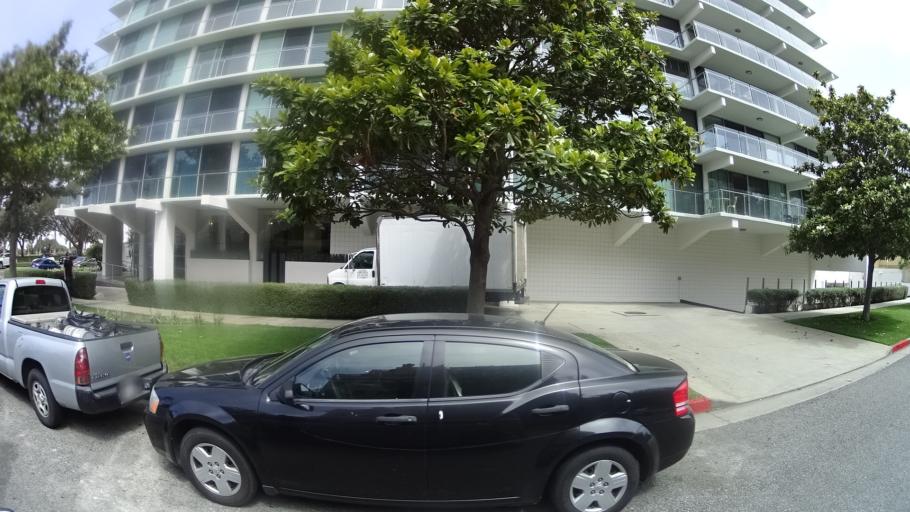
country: US
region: California
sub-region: Los Angeles County
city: Santa Monica
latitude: 34.0242
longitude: -118.5094
